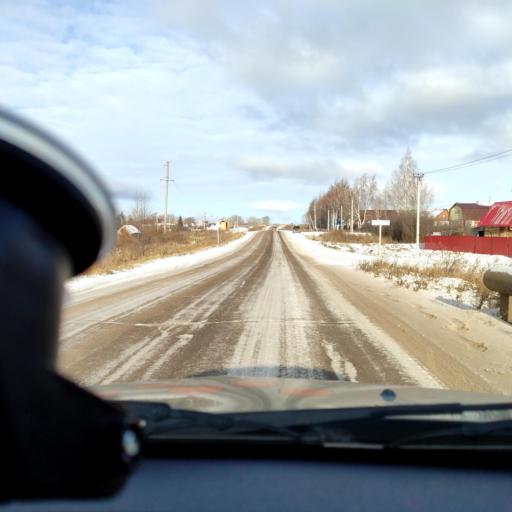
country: RU
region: Bashkortostan
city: Mikhaylovka
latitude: 54.7991
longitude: 55.7799
